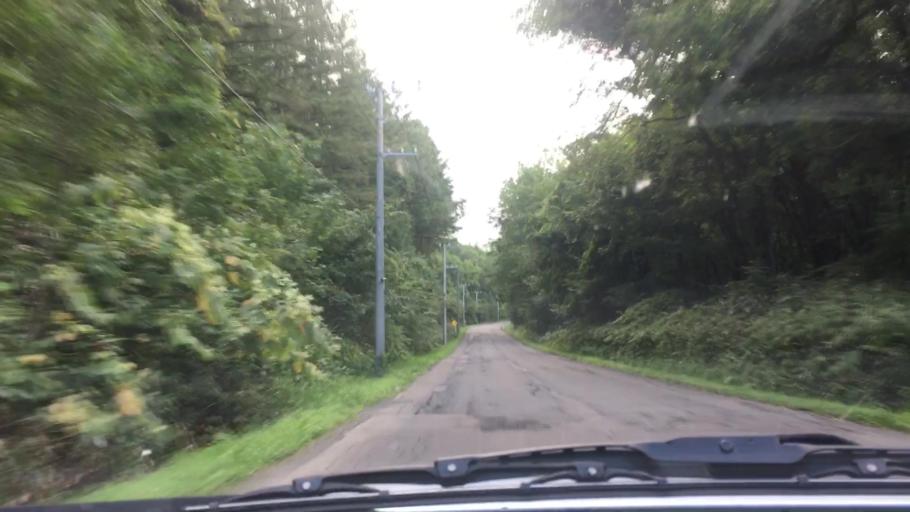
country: JP
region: Hokkaido
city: Otofuke
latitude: 43.1441
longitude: 142.8783
